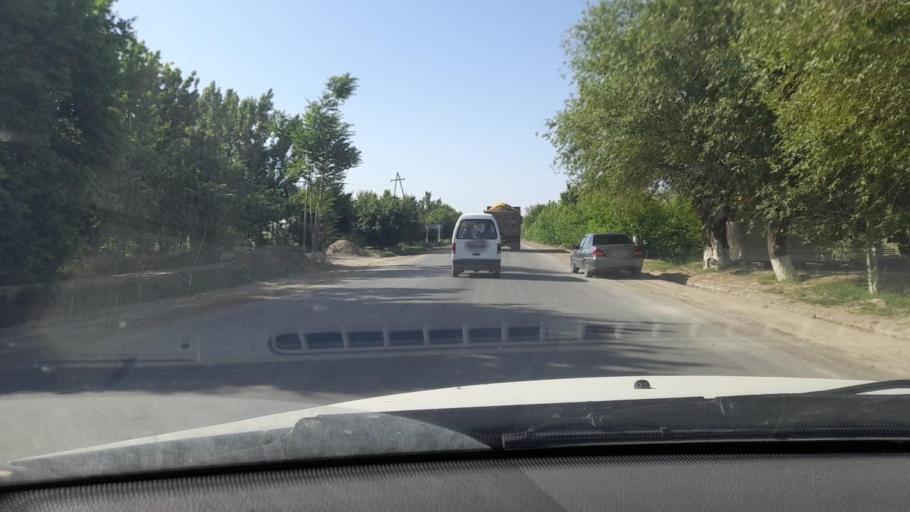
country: UZ
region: Bukhara
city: Romiton
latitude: 40.0554
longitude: 64.3280
